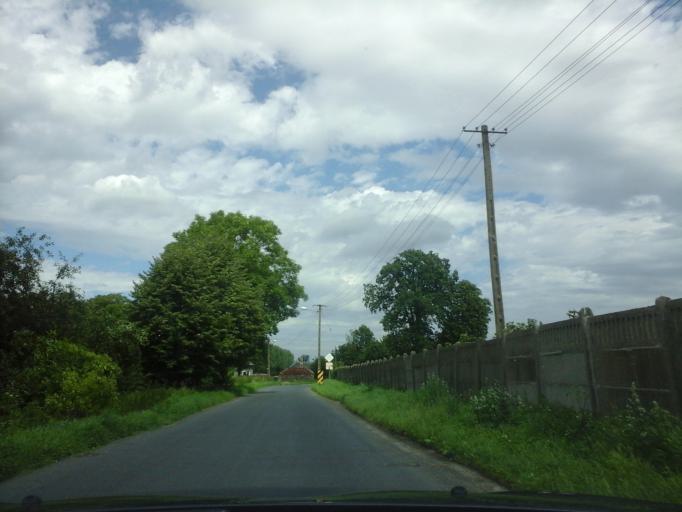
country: PL
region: West Pomeranian Voivodeship
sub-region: Powiat choszczenski
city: Recz
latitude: 53.2909
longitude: 15.4965
